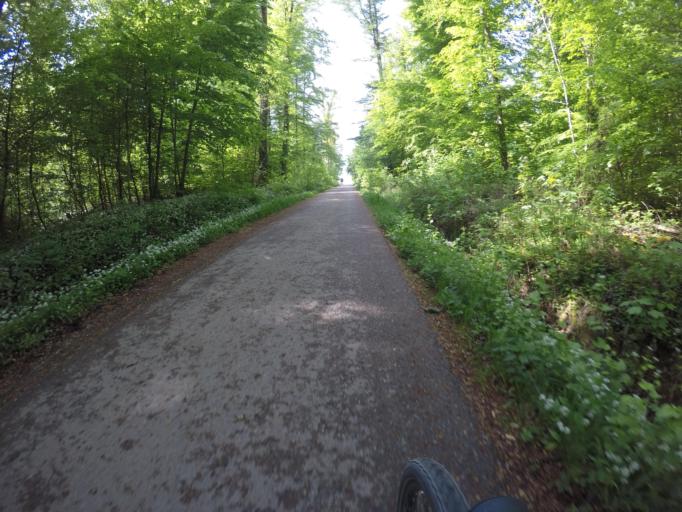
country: DE
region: Baden-Wuerttemberg
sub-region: Tuebingen Region
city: Tuebingen
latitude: 48.5490
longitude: 9.0340
